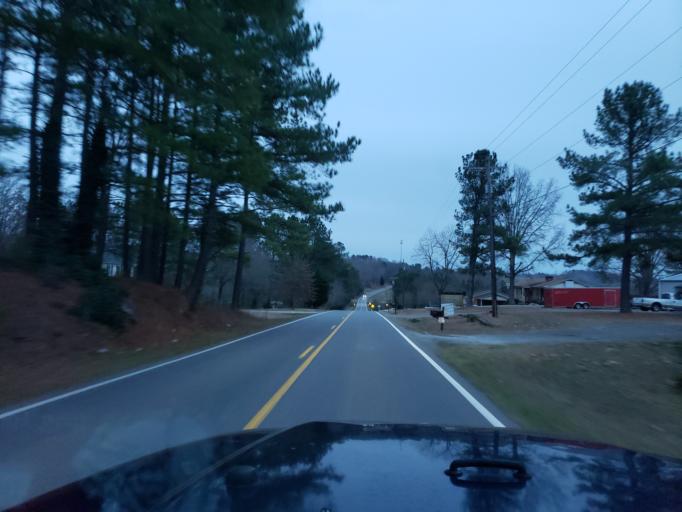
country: US
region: North Carolina
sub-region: Cleveland County
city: White Plains
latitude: 35.2255
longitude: -81.4590
